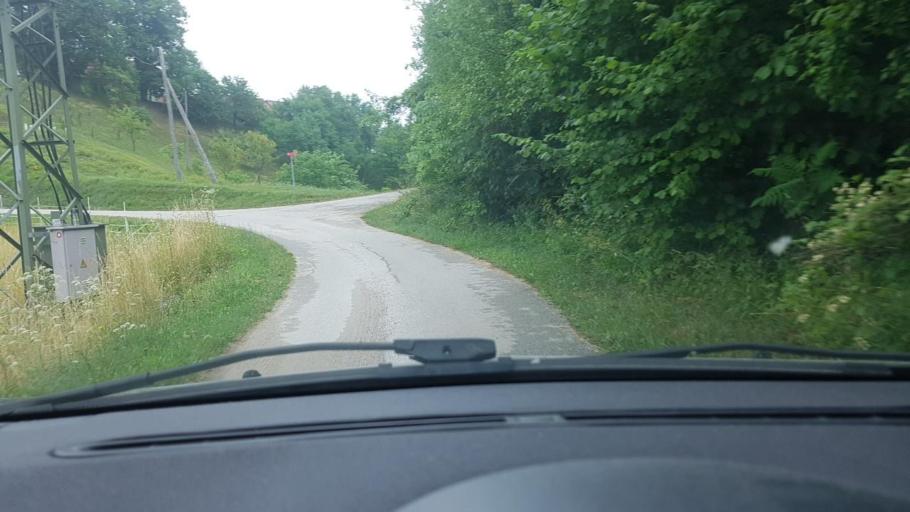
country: SI
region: Videm
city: Videm pri Ptuju
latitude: 46.3351
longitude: 15.9165
